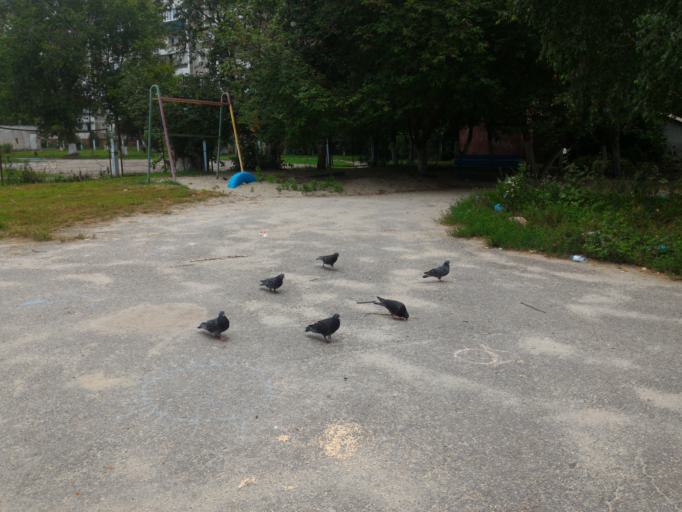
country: RU
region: Kursk
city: Kursk
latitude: 51.7335
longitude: 36.1300
